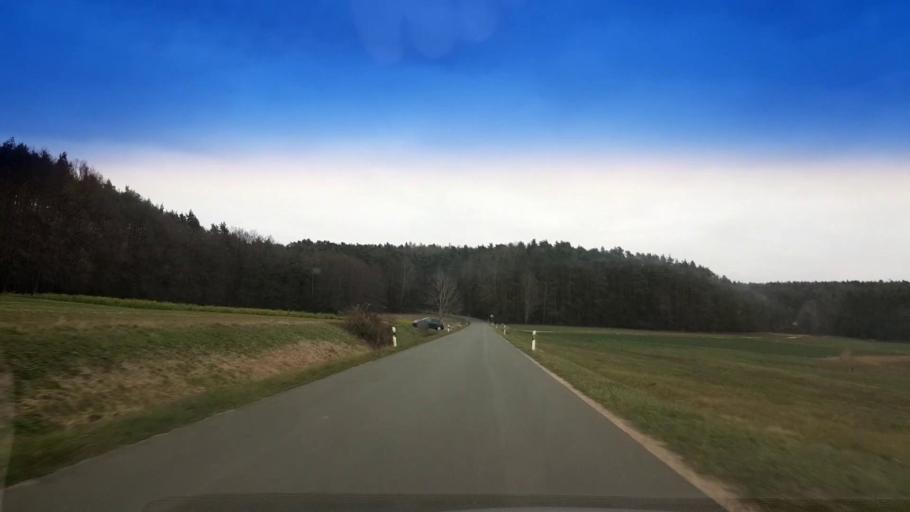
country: DE
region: Bavaria
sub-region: Upper Franconia
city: Pettstadt
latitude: 49.7739
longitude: 10.9161
